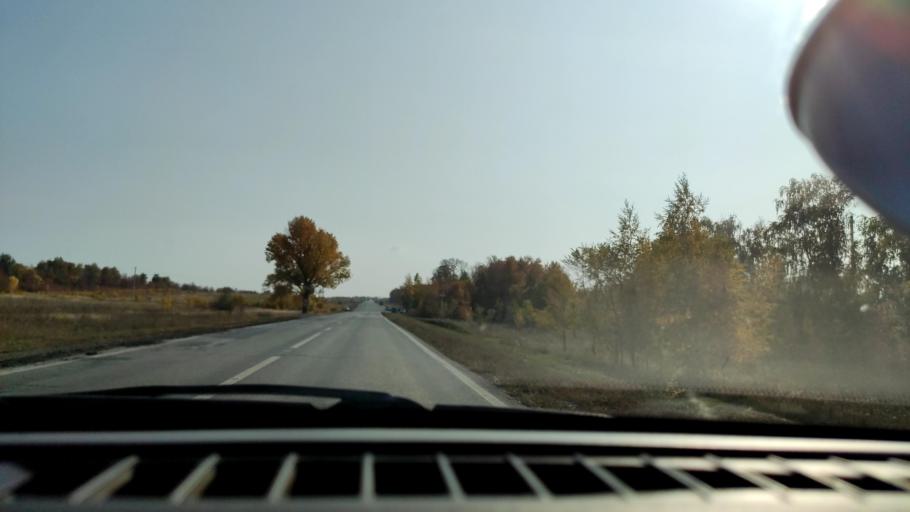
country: RU
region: Samara
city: Dubovyy Umet
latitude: 53.0965
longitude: 50.3496
